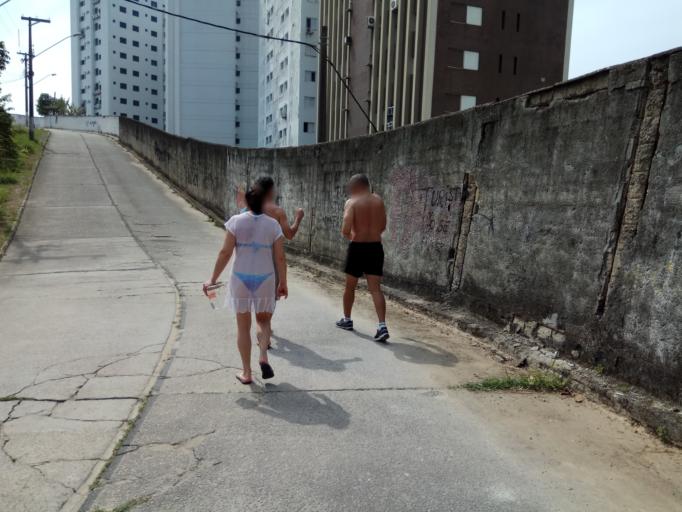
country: BR
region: Sao Paulo
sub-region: Guaruja
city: Guaruja
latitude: -23.9960
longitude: -46.2500
